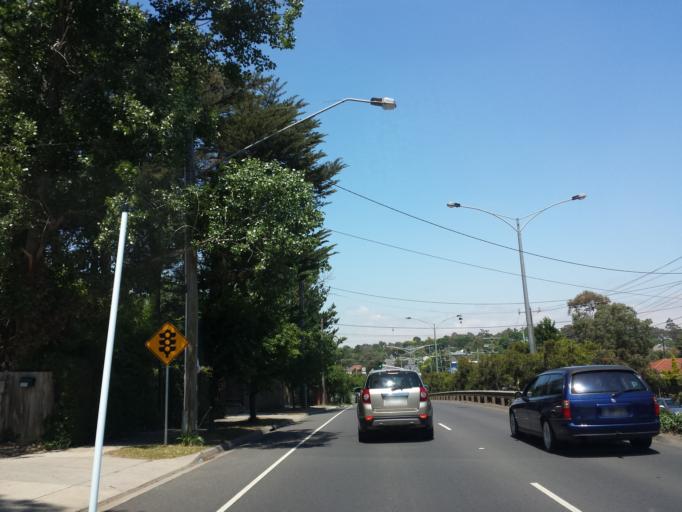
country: AU
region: Victoria
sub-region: Maroondah
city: Croydon North
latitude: -37.8013
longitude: 145.2896
